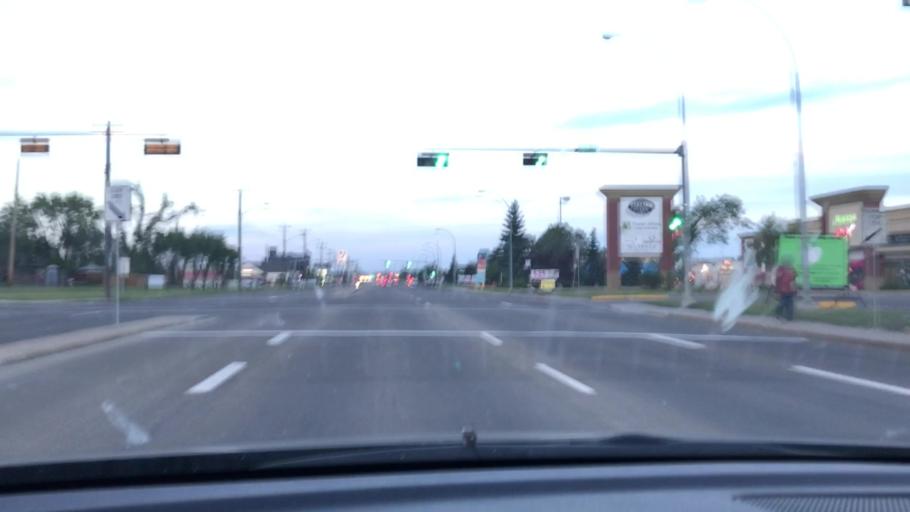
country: CA
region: Alberta
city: Edmonton
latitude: 53.4882
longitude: -113.5009
